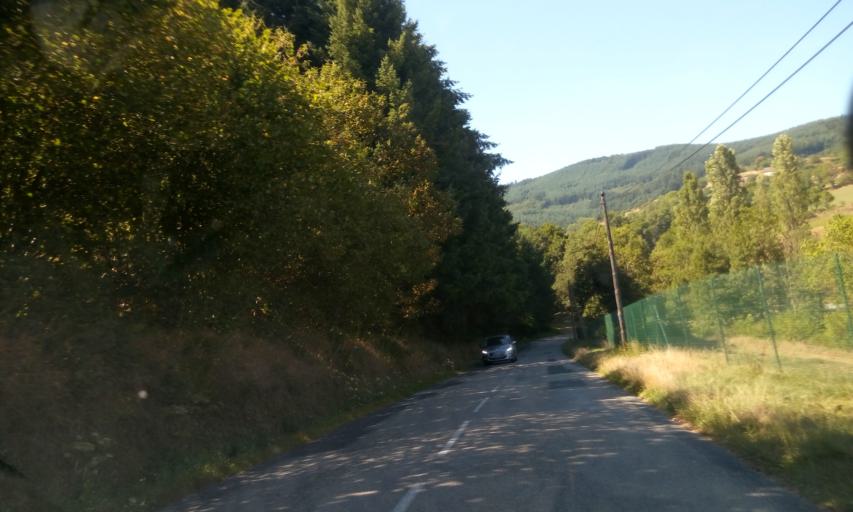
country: FR
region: Rhone-Alpes
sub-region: Departement du Rhone
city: Grandris
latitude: 46.0047
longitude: 4.4504
